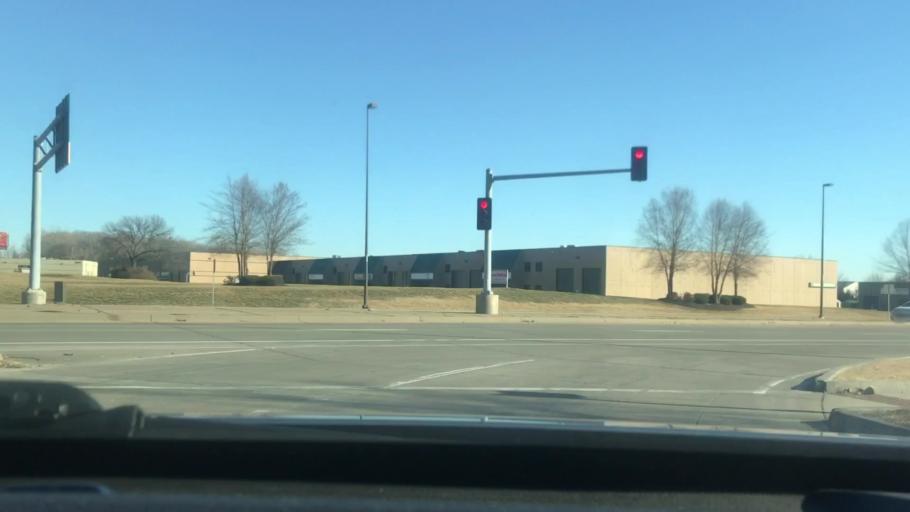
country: US
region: Missouri
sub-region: Clay County
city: North Kansas City
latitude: 39.1497
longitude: -94.5360
